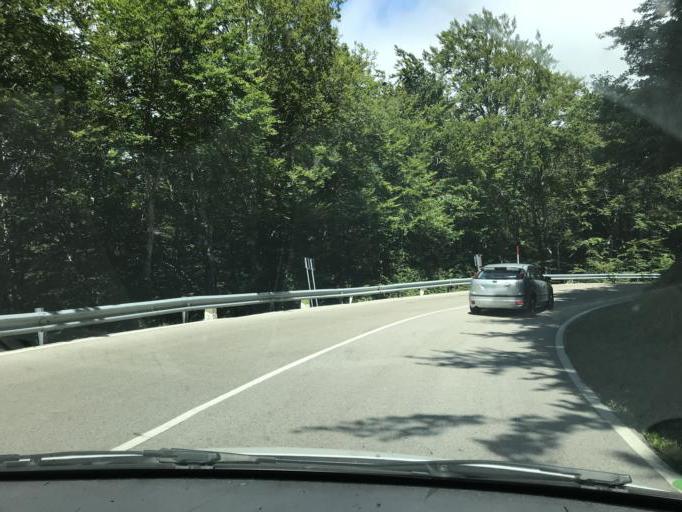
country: ES
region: Cantabria
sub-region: Provincia de Cantabria
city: Cabezon de Liebana
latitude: 43.0709
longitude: -4.4754
